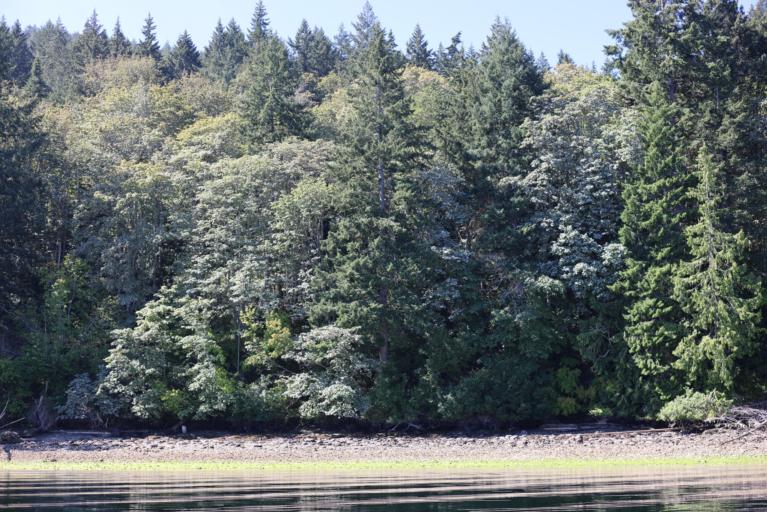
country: CA
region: British Columbia
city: North Cowichan
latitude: 48.8537
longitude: -123.6101
